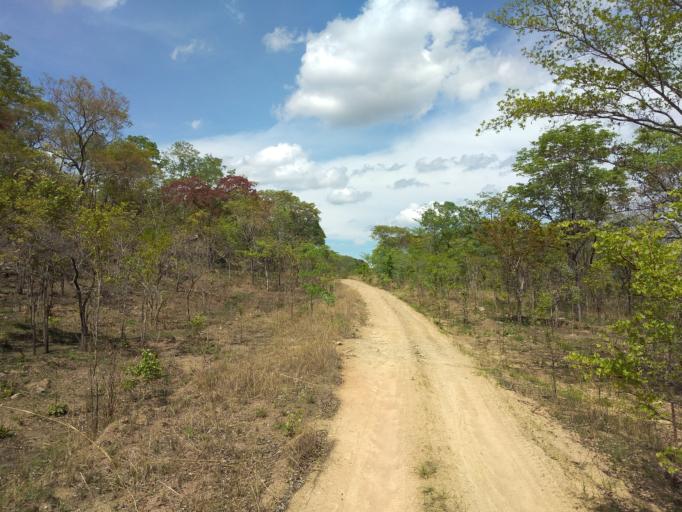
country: ZM
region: Eastern
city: Nyimba
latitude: -14.1242
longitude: 30.0935
